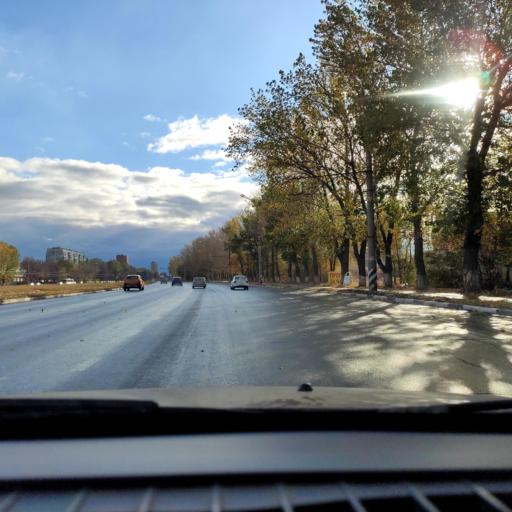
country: RU
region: Samara
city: Tol'yatti
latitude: 53.5222
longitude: 49.2589
